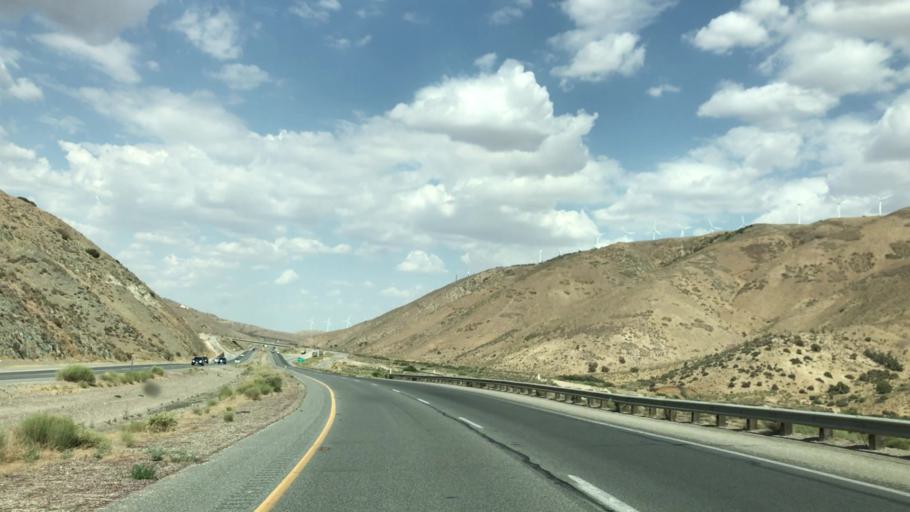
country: US
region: California
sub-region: Kern County
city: Mojave
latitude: 35.0971
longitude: -118.3023
